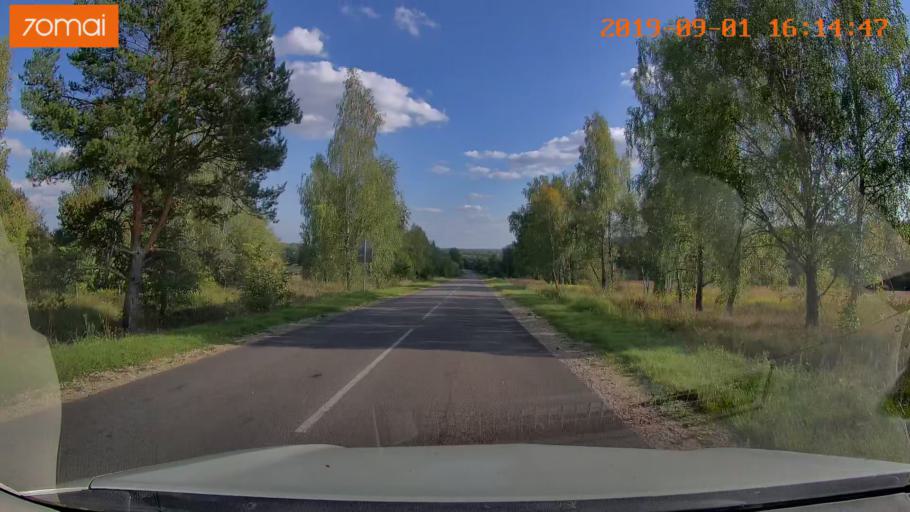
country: RU
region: Kaluga
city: Maloyaroslavets
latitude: 54.9288
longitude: 36.4720
